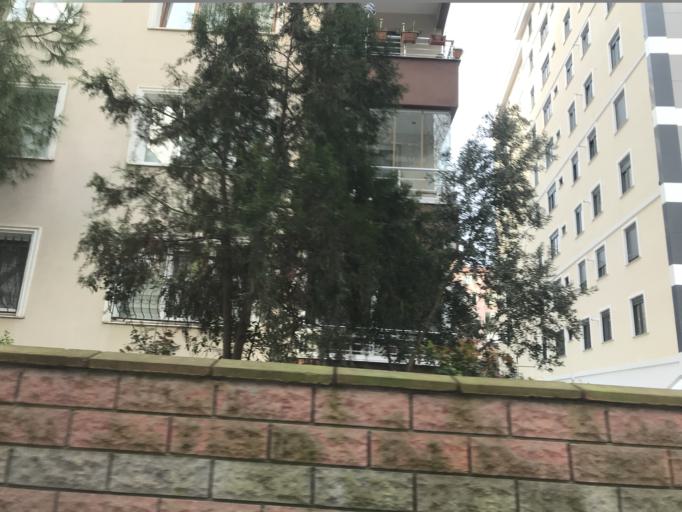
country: TR
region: Istanbul
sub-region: Atasehir
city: Atasehir
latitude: 40.9618
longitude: 29.0973
